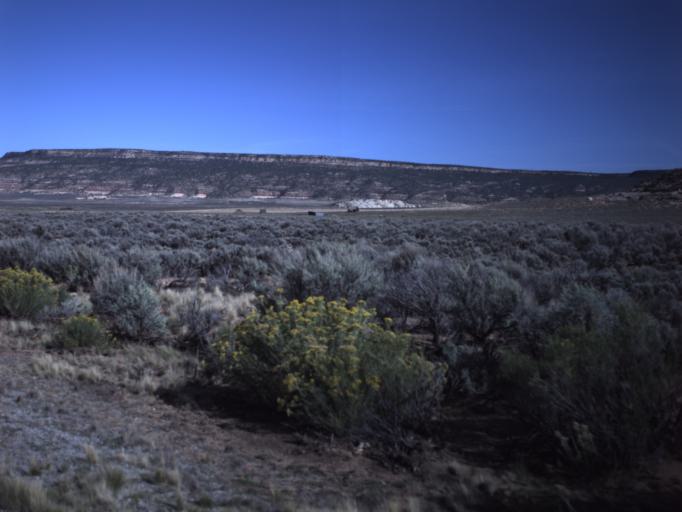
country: US
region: Utah
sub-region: San Juan County
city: Monticello
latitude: 38.0631
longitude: -109.3914
